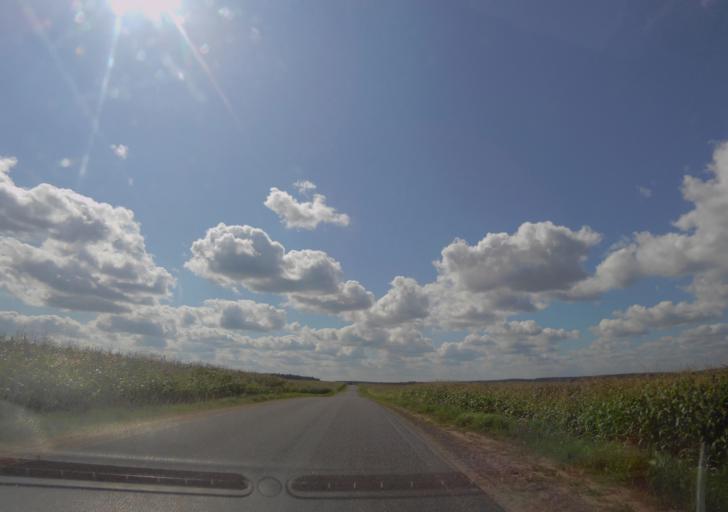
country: BY
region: Minsk
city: Horad Barysaw
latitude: 54.3793
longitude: 28.4788
